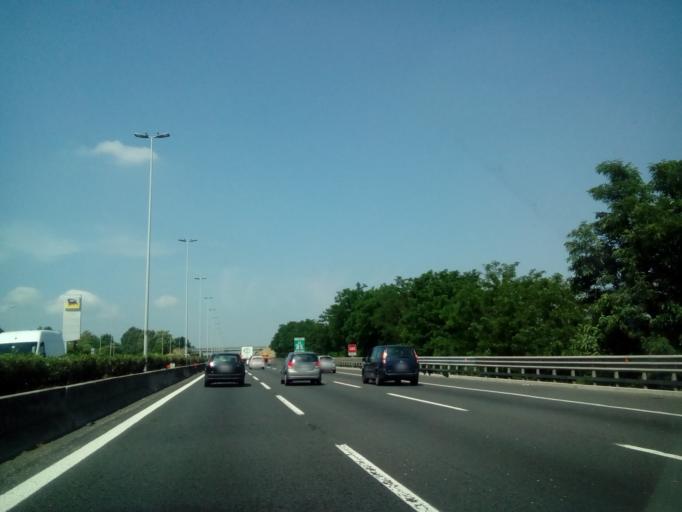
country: IT
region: Latium
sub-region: Citta metropolitana di Roma Capitale
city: Borgo Lotti
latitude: 41.7947
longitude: 12.5189
